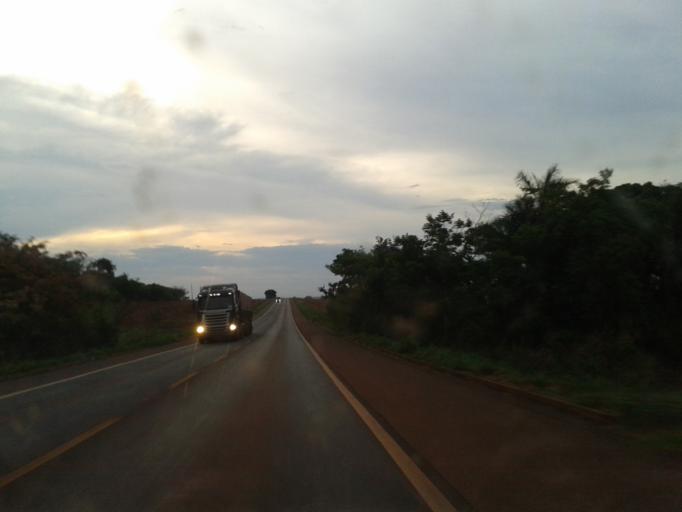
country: BR
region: Goias
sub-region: Santa Helena De Goias
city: Santa Helena de Goias
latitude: -17.9028
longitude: -50.6384
